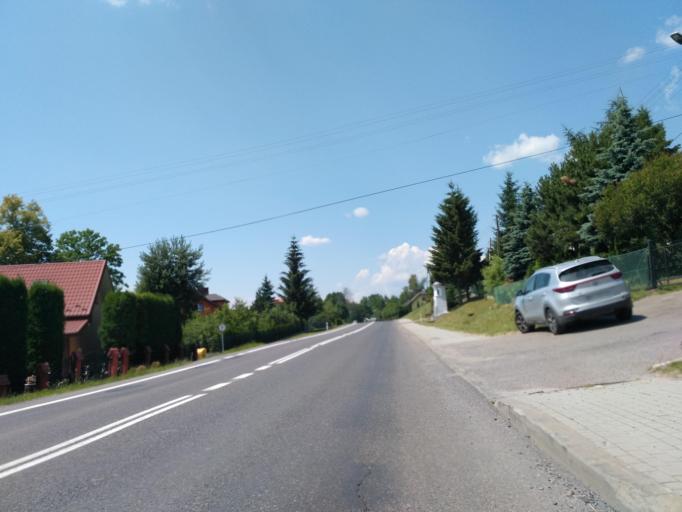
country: PL
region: Subcarpathian Voivodeship
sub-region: Powiat sanocki
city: Strachocina
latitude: 49.6224
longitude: 22.1051
